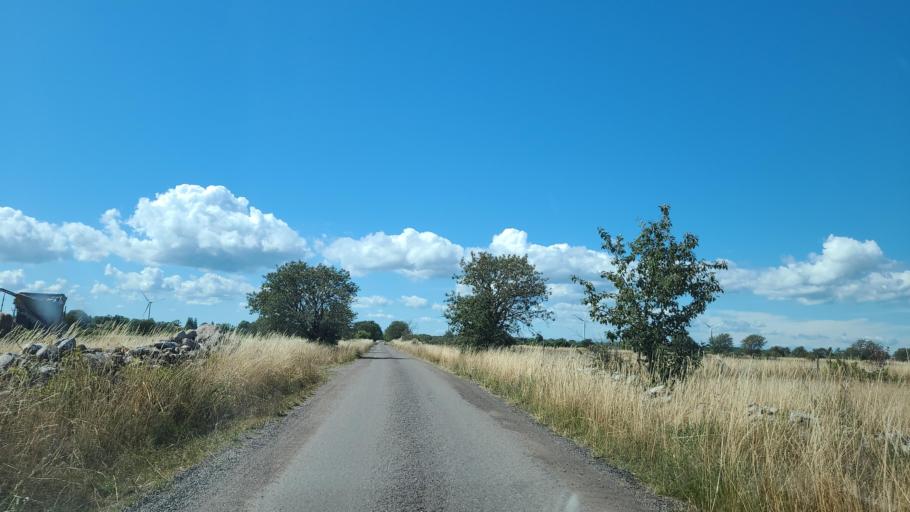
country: SE
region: Kalmar
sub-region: Morbylanga Kommun
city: Sodra Sandby
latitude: 56.7110
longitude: 16.7205
